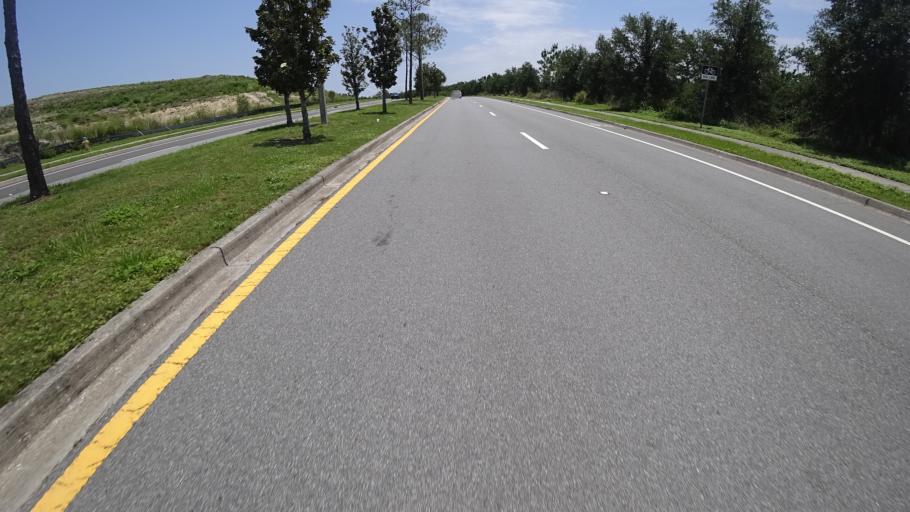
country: US
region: Florida
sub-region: Sarasota County
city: Desoto Lakes
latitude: 27.4259
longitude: -82.4964
